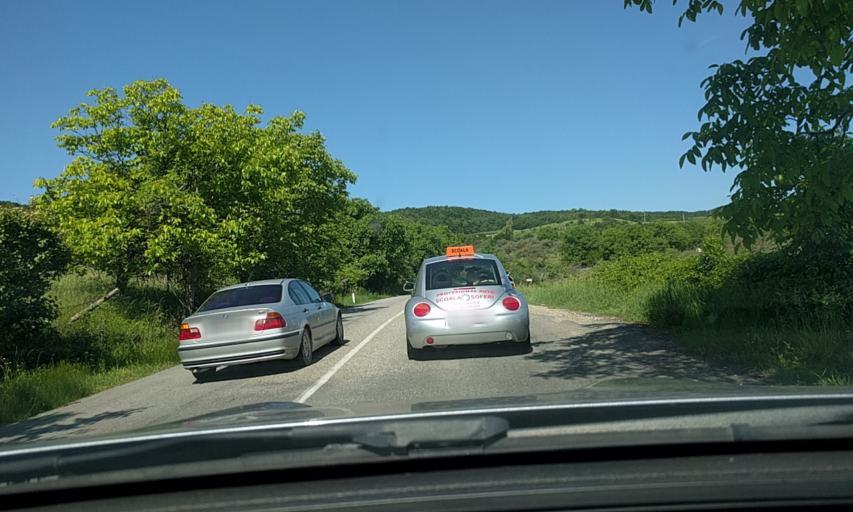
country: RO
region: Bistrita-Nasaud
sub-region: Municipiul Bistrita
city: Unirea
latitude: 47.1753
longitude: 24.4931
